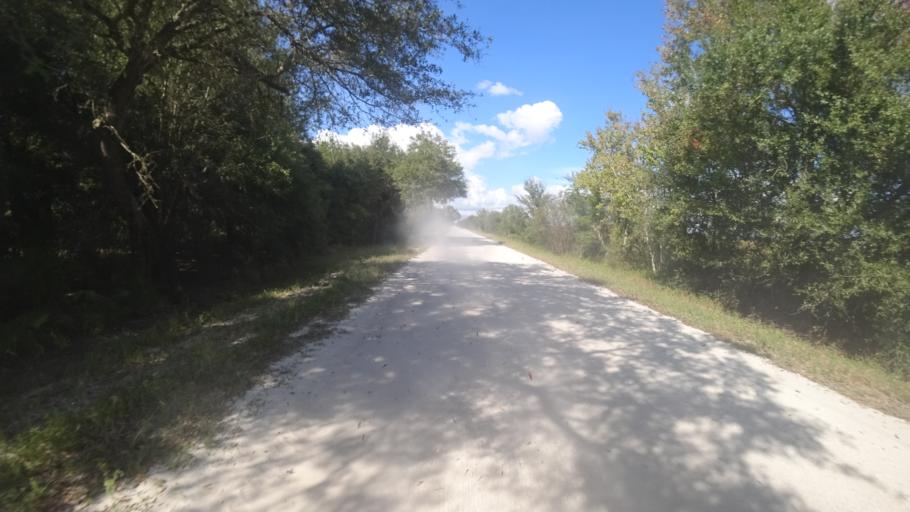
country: US
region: Florida
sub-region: DeSoto County
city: Arcadia
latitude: 27.3133
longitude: -82.0805
